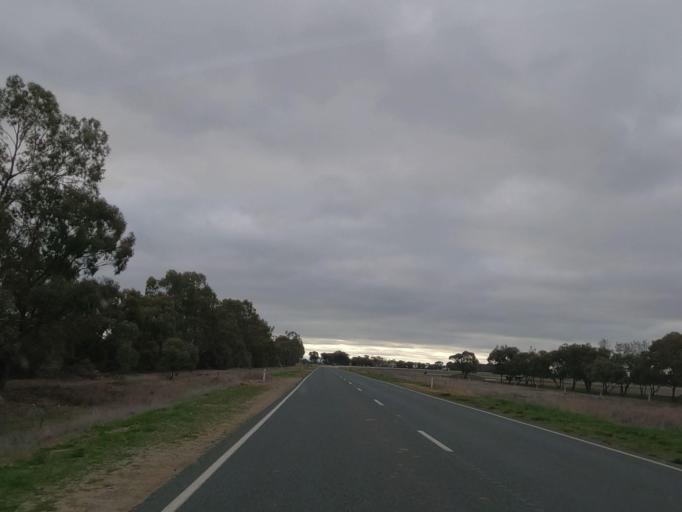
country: AU
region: Victoria
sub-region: Swan Hill
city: Swan Hill
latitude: -35.9343
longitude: 143.9354
